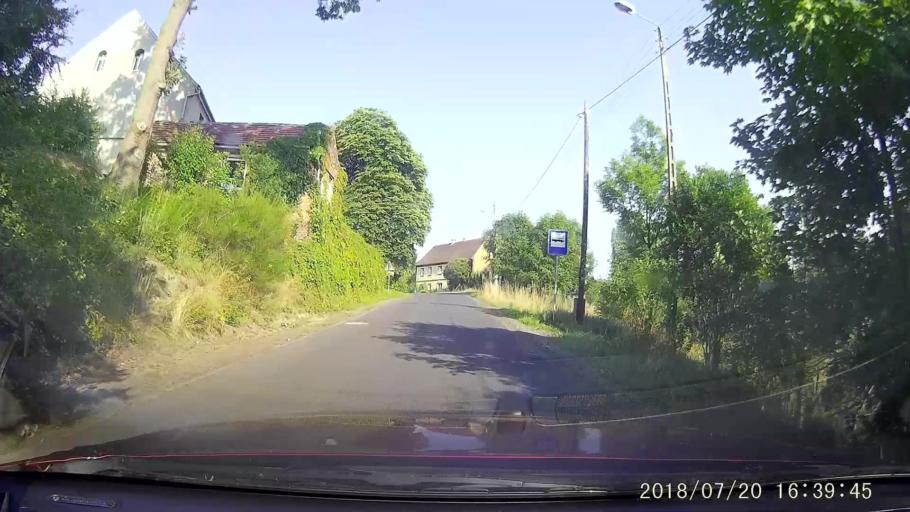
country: PL
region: Lower Silesian Voivodeship
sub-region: Powiat lubanski
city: Siekierczyn
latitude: 51.0863
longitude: 15.1413
